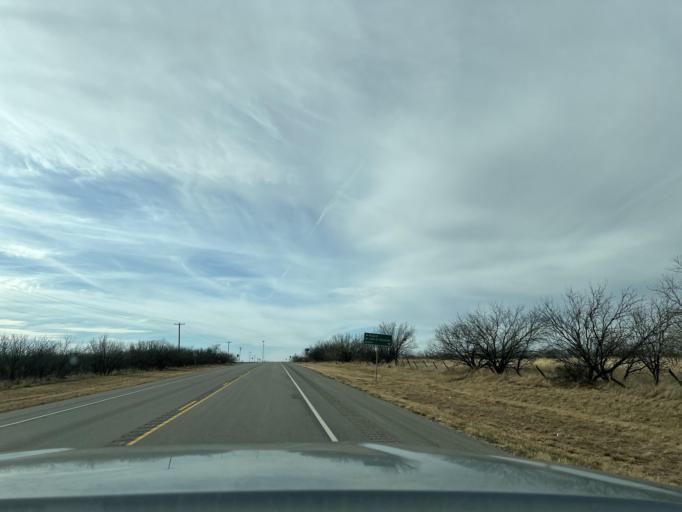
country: US
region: Texas
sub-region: Jones County
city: Anson
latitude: 32.7506
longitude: -99.7103
